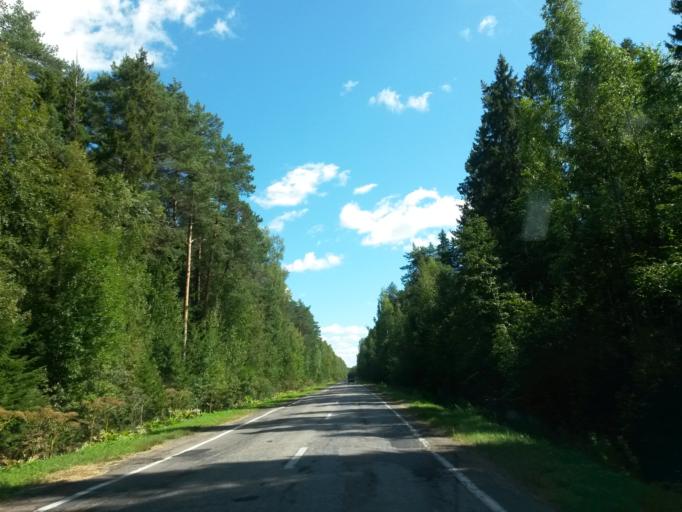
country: RU
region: Jaroslavl
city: Konstantinovskiy
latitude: 57.8043
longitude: 39.7818
